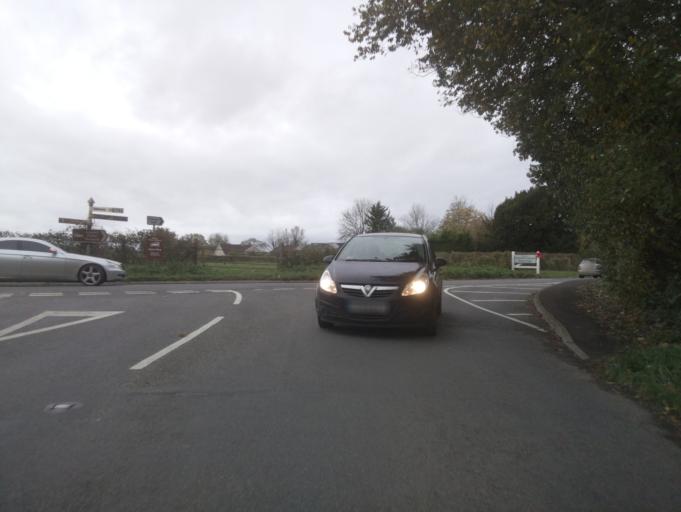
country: GB
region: England
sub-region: Somerset
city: Yeovil
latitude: 50.9967
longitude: -2.5839
